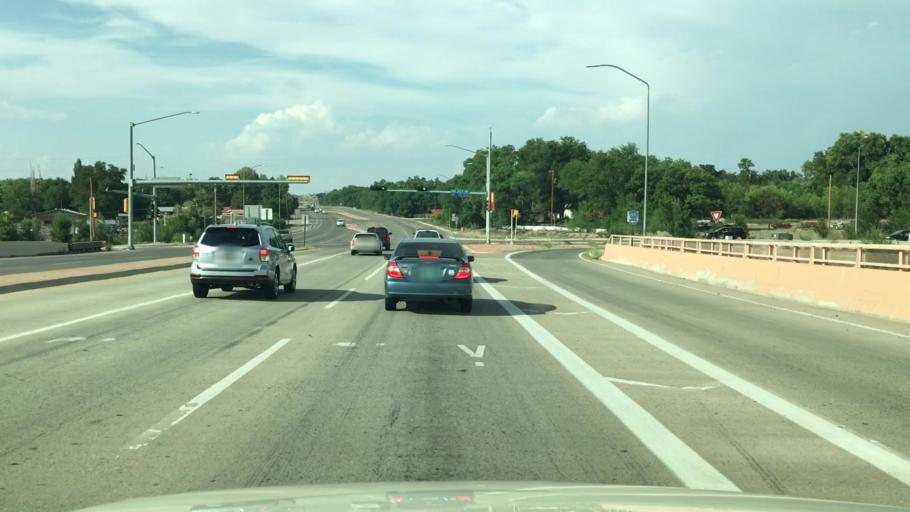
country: US
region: New Mexico
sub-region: Santa Fe County
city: Pojoaque
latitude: 35.8966
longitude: -106.0214
